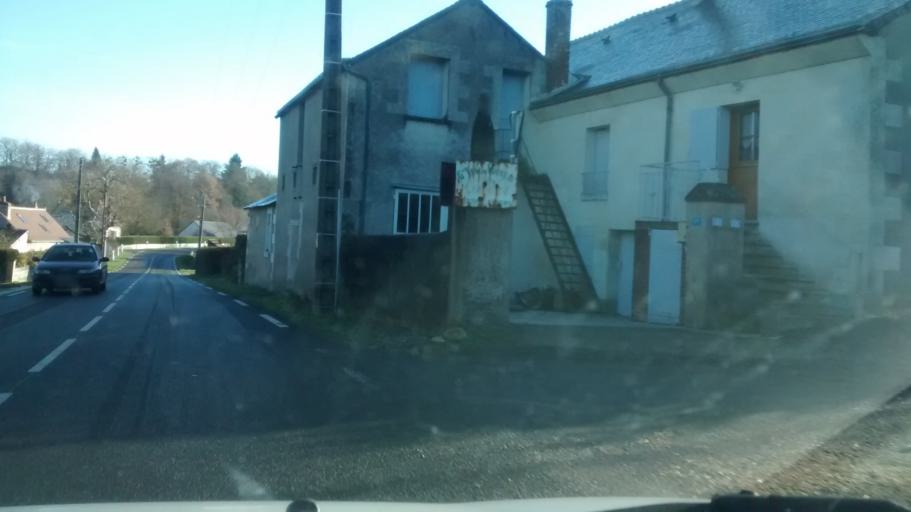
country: FR
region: Centre
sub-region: Departement d'Indre-et-Loire
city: Reugny
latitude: 47.4848
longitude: 0.8594
